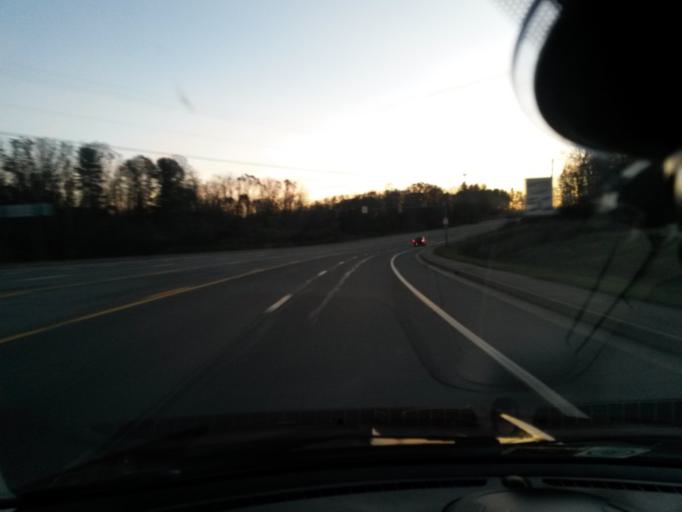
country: US
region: West Virginia
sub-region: Raleigh County
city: Stanaford
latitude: 37.7824
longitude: -81.1521
